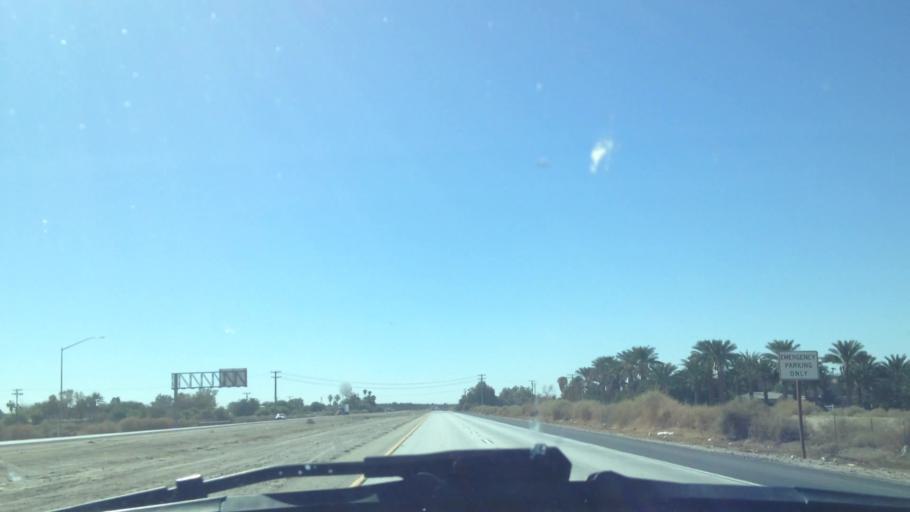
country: US
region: California
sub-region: Riverside County
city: Thermal
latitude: 33.6399
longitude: -116.1314
